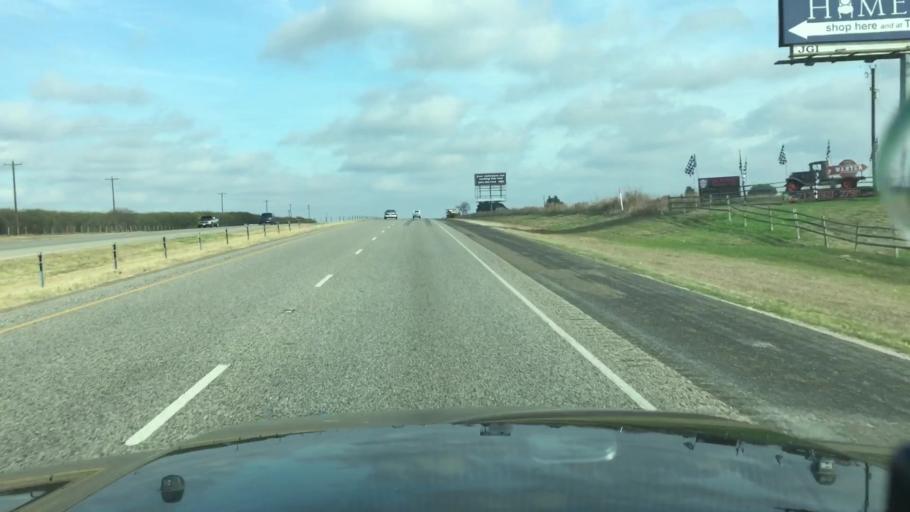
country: US
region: Texas
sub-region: Washington County
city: Brenham
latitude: 30.1402
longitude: -96.2983
